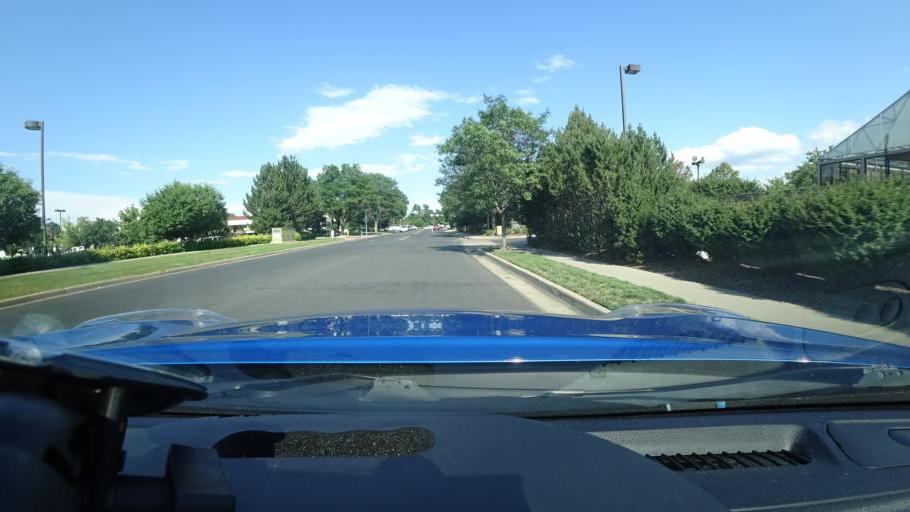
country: US
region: Colorado
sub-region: Adams County
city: Aurora
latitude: 39.6857
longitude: -104.8677
